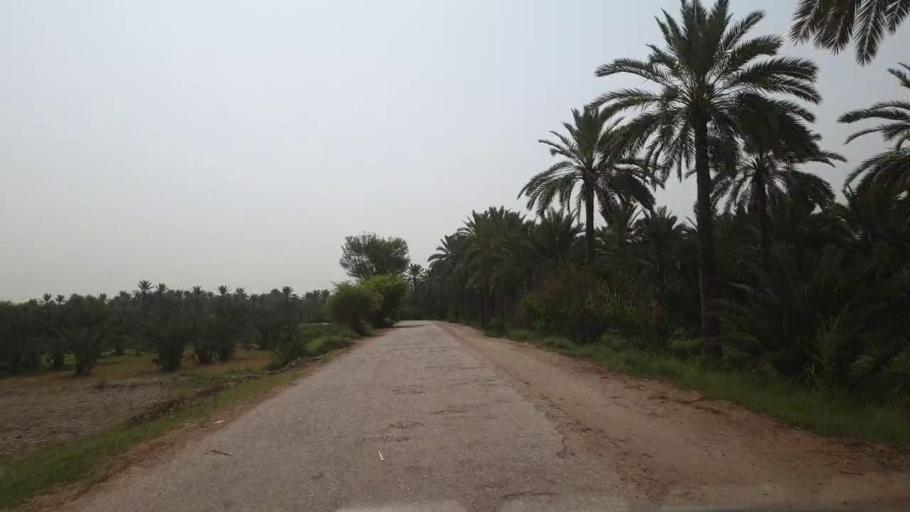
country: PK
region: Sindh
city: Gambat
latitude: 27.4079
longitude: 68.5524
